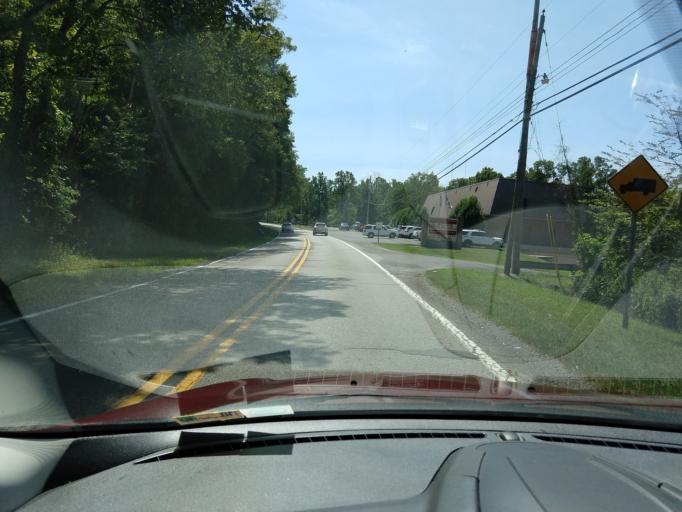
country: US
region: West Virginia
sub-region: Monongalia County
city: Westover
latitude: 39.6282
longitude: -79.9789
